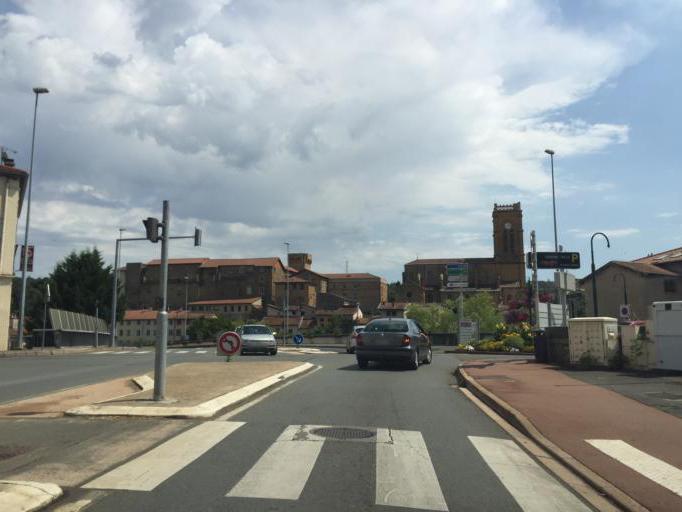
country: FR
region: Rhone-Alpes
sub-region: Departement du Rhone
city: Saint-Germain-Nuelles
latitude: 45.8373
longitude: 4.6167
